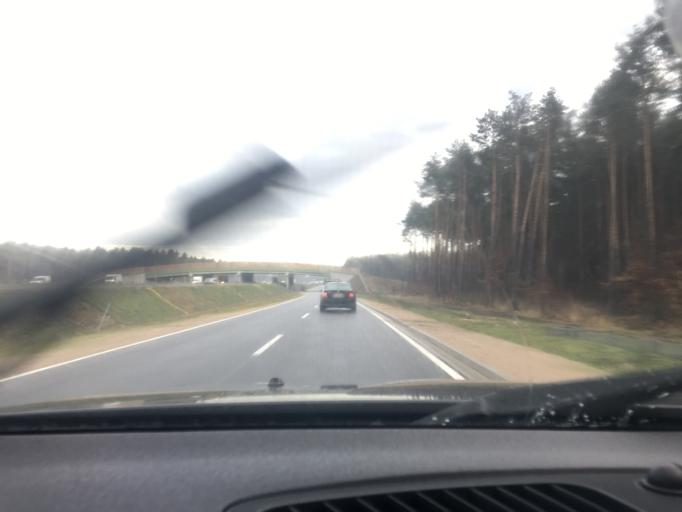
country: PL
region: Swietokrzyskie
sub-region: Powiat jedrzejowski
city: Jedrzejow
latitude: 50.6757
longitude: 20.3495
